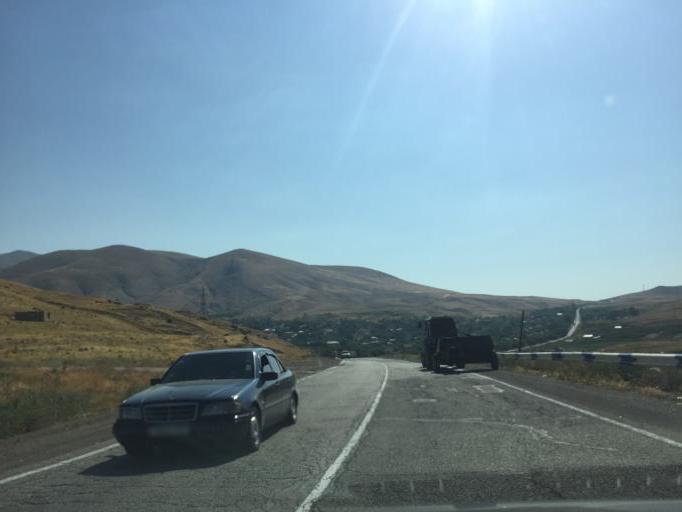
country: AM
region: Ararat
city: Zangakatun
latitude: 39.8173
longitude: 45.0242
